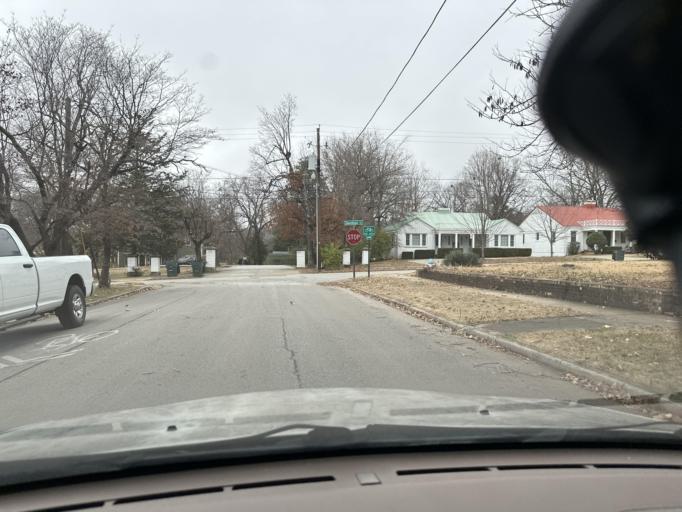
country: US
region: Arkansas
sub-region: Washington County
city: Fayetteville
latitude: 36.0710
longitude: -94.1561
